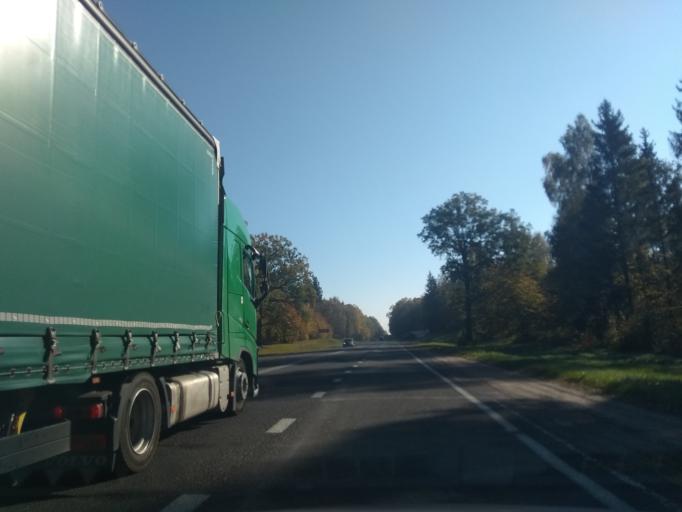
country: BY
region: Grodnenskaya
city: Slonim
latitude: 53.1103
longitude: 25.1707
